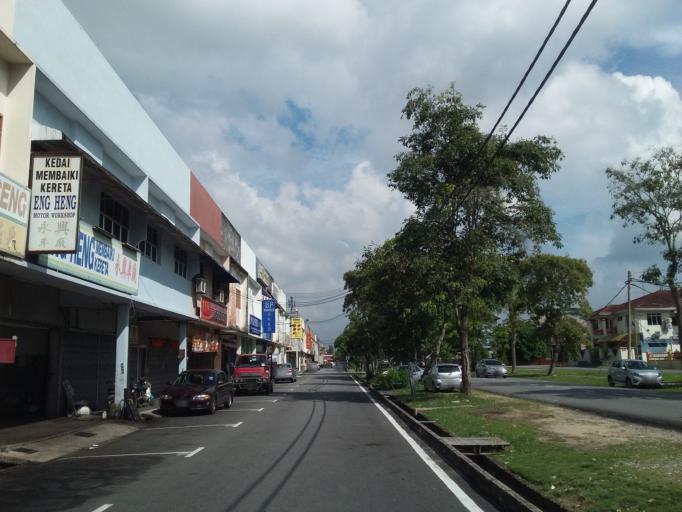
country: MY
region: Johor
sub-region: Daerah Batu Pahat
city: Batu Pahat
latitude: 1.8416
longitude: 102.9291
